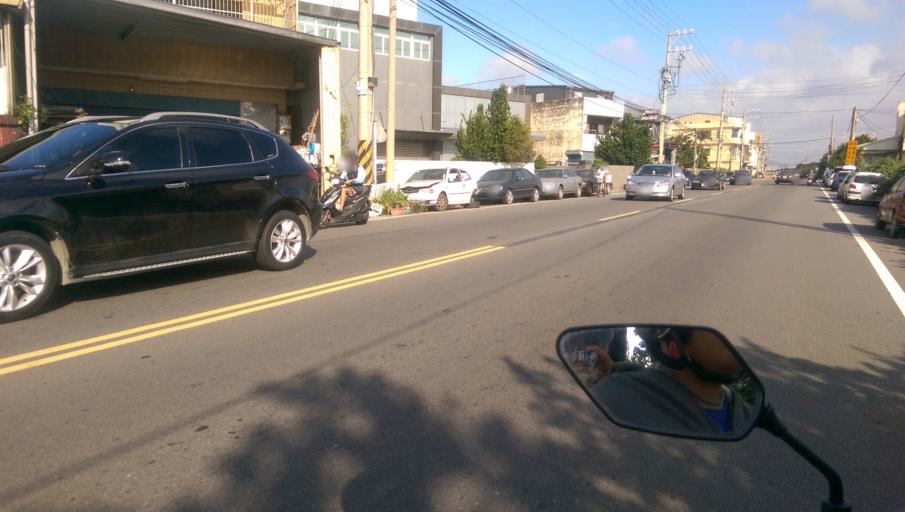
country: TW
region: Taiwan
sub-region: Hsinchu
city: Hsinchu
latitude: 24.8327
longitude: 120.9504
